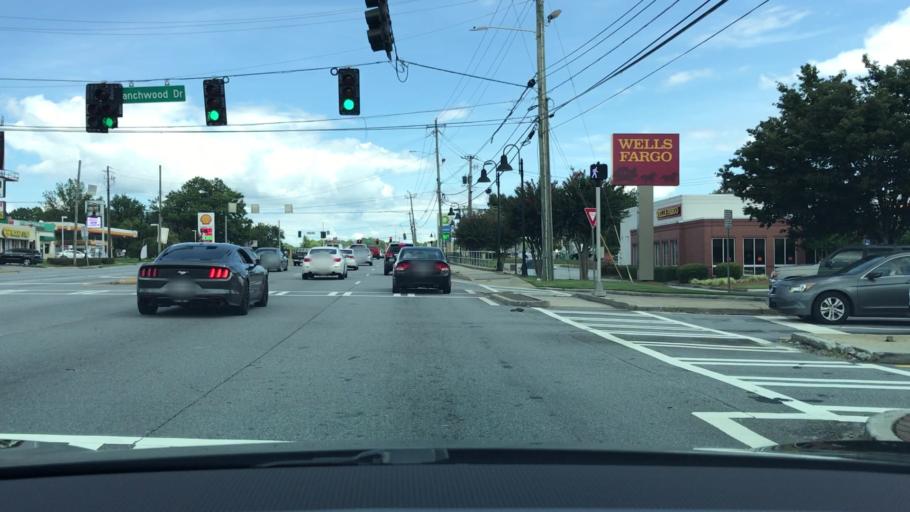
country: US
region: Georgia
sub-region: DeKalb County
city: Tucker
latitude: 33.8464
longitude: -84.2519
